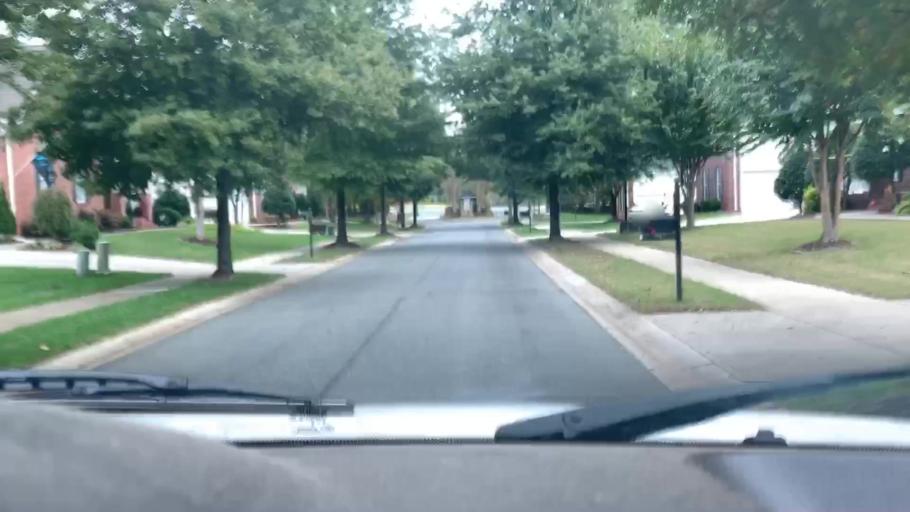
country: US
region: North Carolina
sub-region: Mecklenburg County
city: Huntersville
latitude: 35.4267
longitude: -80.8745
